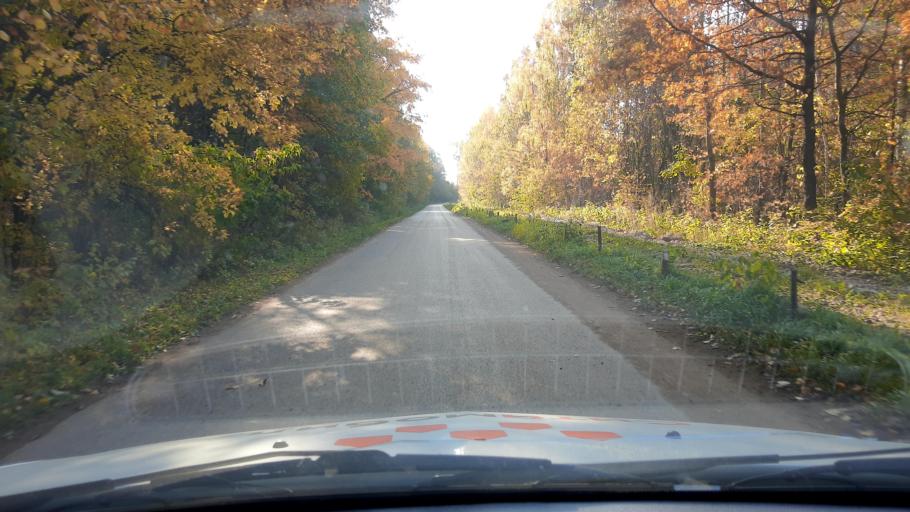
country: RU
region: Bashkortostan
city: Ufa
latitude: 54.6625
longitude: 56.0596
